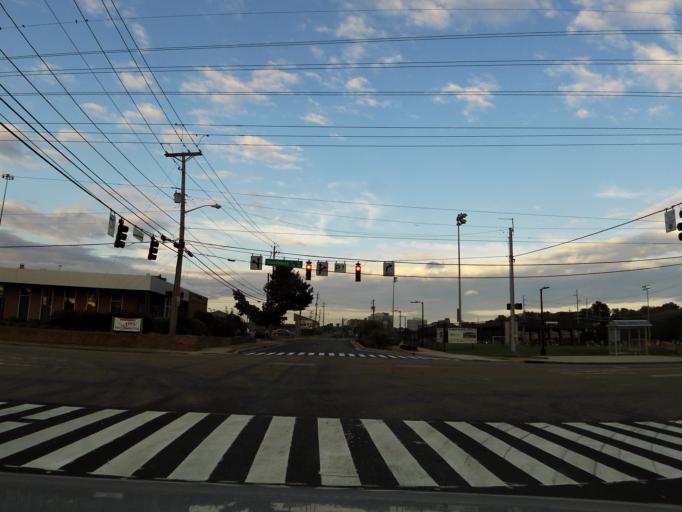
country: US
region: Tennessee
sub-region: Knox County
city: Knoxville
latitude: 35.9631
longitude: -83.9361
